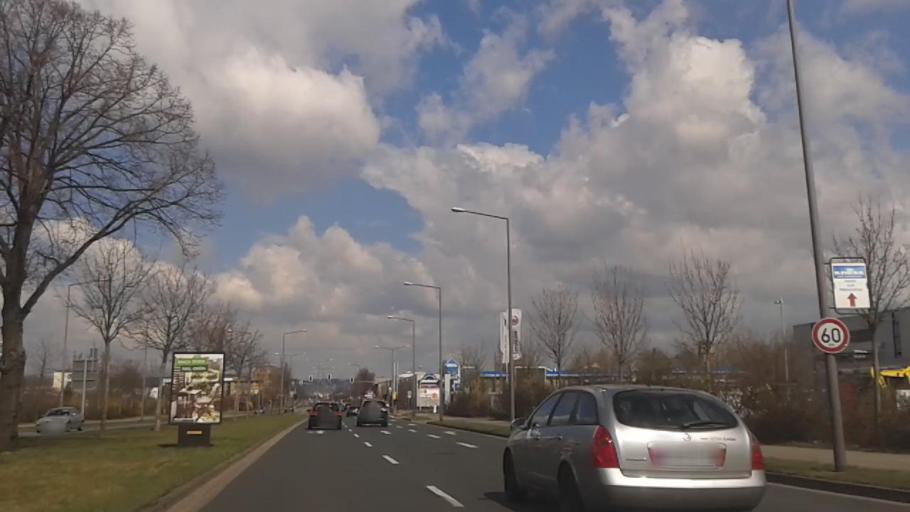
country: DE
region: Saxony
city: Radebeul
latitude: 51.0679
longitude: 13.6895
